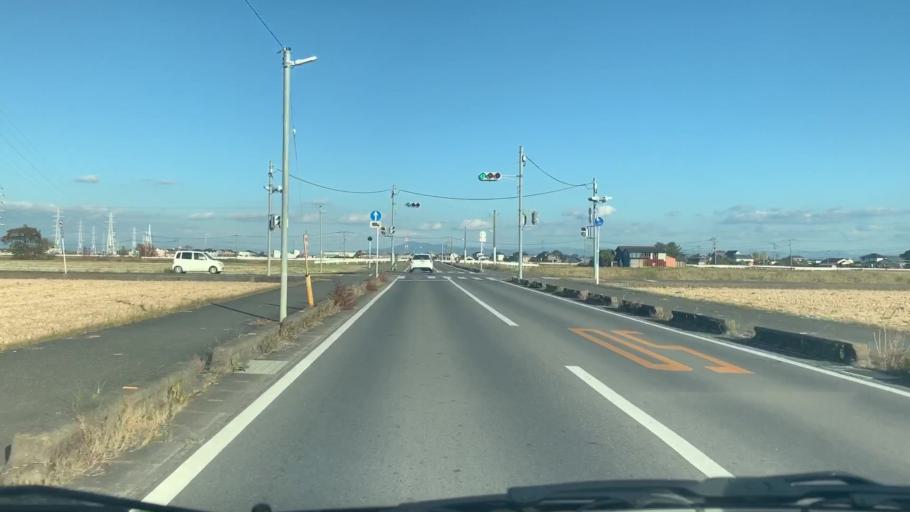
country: JP
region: Saga Prefecture
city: Saga-shi
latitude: 33.2659
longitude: 130.3341
